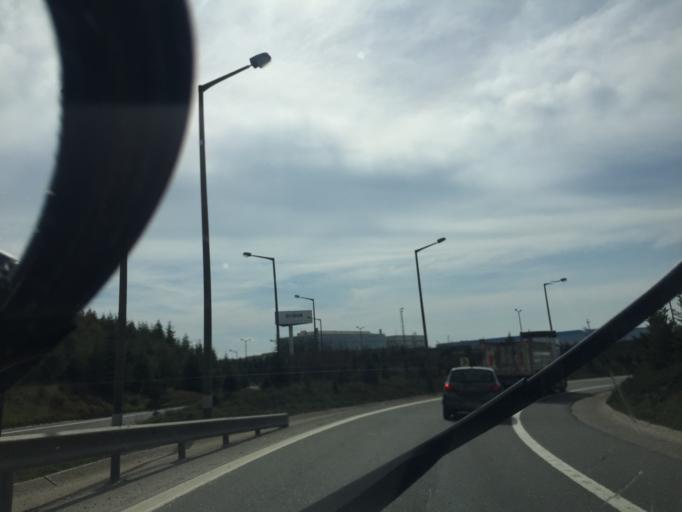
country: TR
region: Kocaeli
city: Balcik
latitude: 40.8700
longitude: 29.3985
